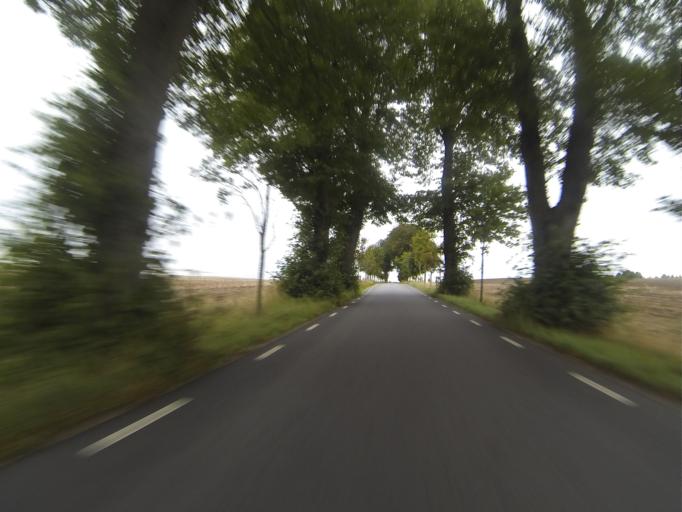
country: SE
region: Skane
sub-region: Lunds Kommun
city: Genarp
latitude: 55.6332
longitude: 13.4072
